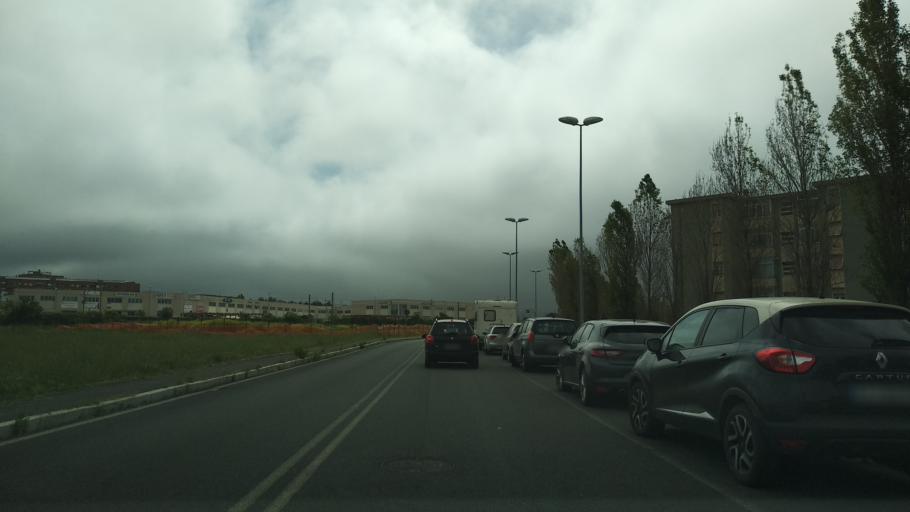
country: IT
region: Tuscany
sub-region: Provincia di Livorno
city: Livorno
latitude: 43.5387
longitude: 10.3317
